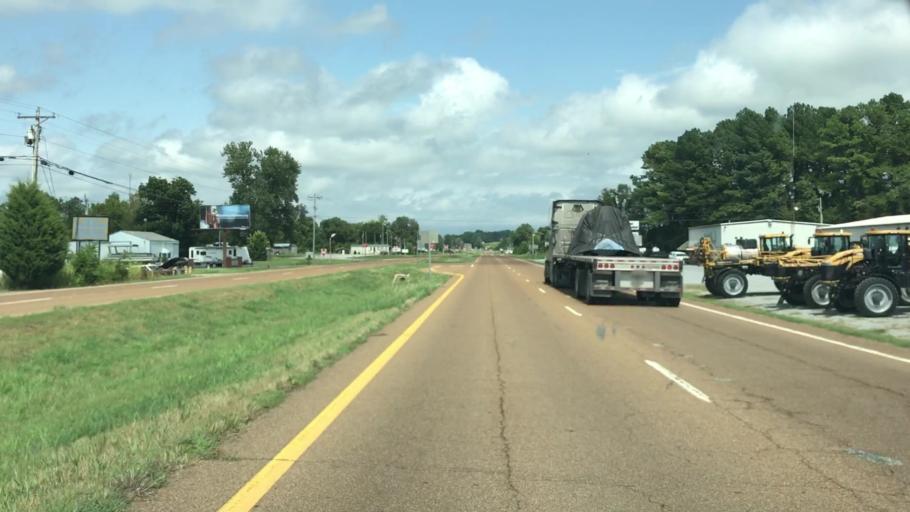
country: US
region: Tennessee
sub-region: Obion County
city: Troy
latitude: 36.3470
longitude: -89.1492
